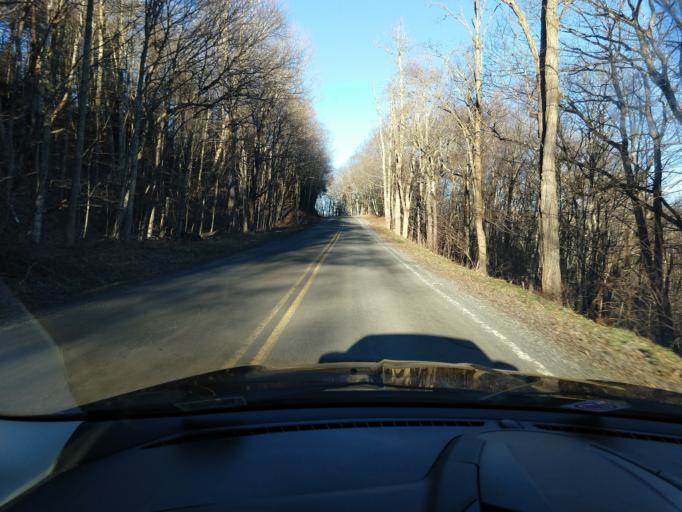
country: US
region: Virginia
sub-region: Highland County
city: Monterey
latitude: 38.4599
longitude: -79.6838
